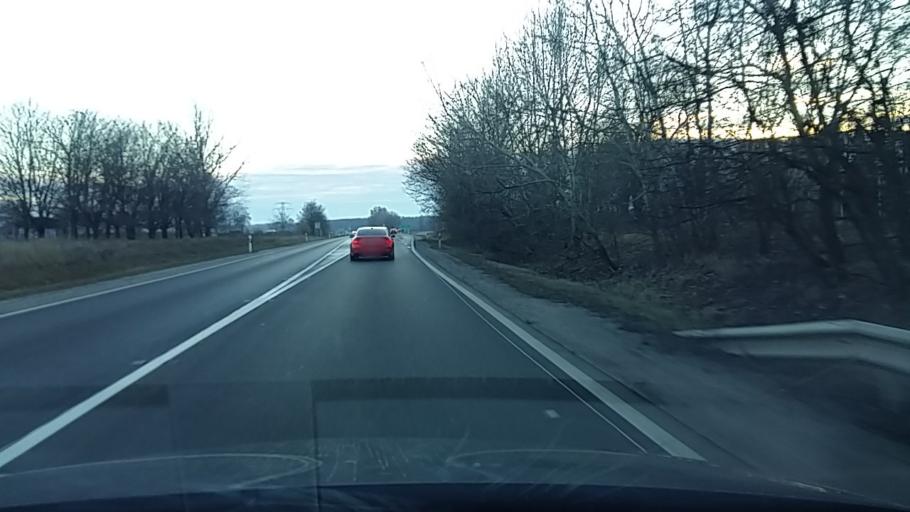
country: HU
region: Hajdu-Bihar
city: Hajduhadhaz
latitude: 47.6855
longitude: 21.6523
